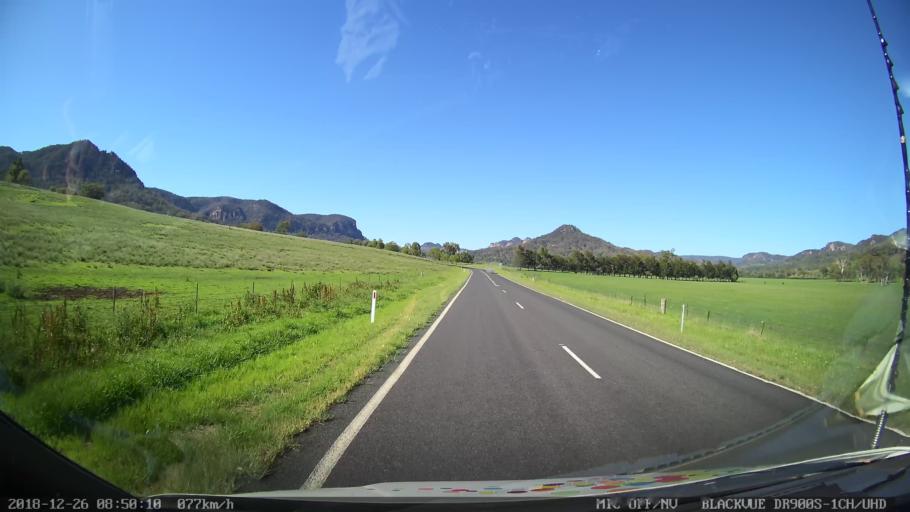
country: AU
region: New South Wales
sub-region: Mid-Western Regional
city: Kandos
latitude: -32.5727
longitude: 150.0966
